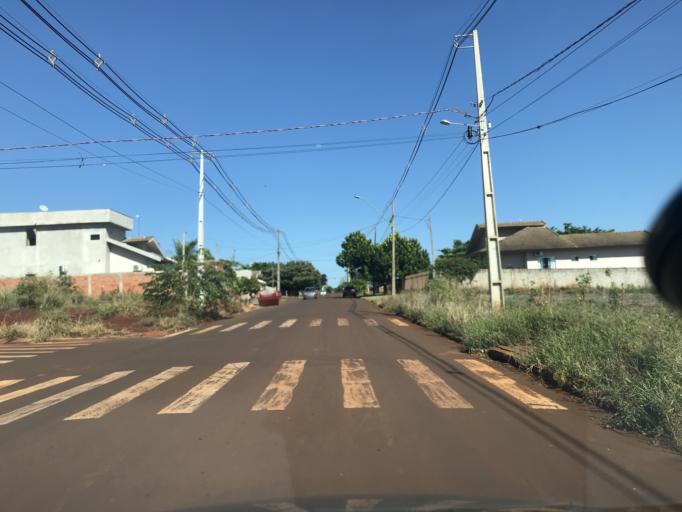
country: BR
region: Parana
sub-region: Palotina
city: Palotina
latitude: -24.2738
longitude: -53.8262
